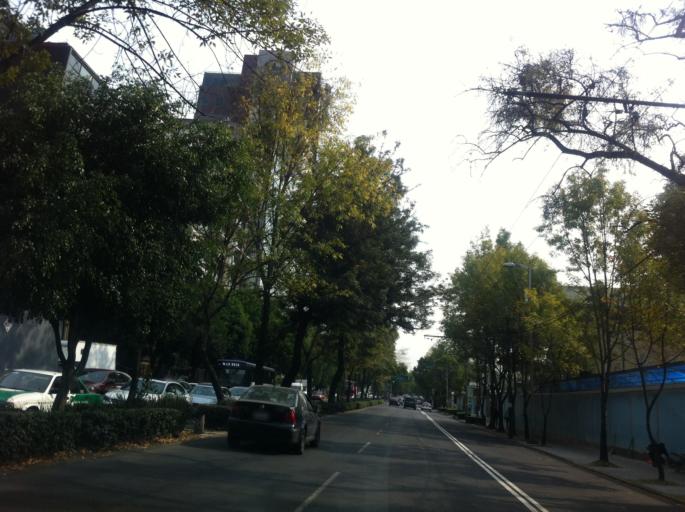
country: MX
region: Mexico City
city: Polanco
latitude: 19.4264
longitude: -99.1791
